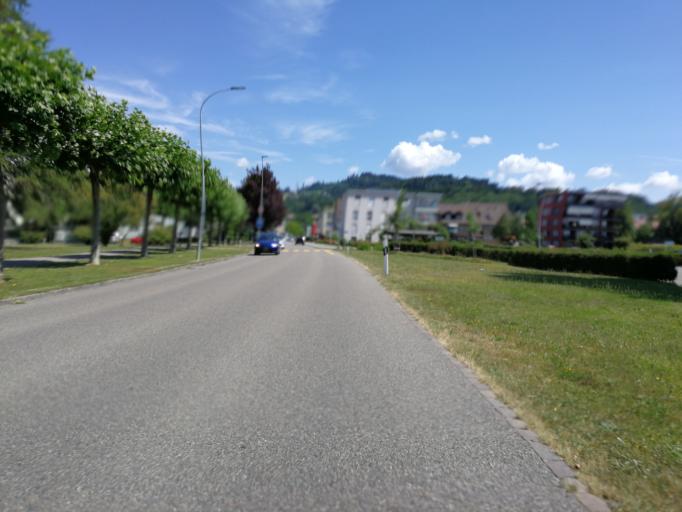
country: CH
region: Zurich
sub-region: Bezirk Hinwil
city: Wetzikon / Kempten
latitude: 47.3276
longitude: 8.8114
